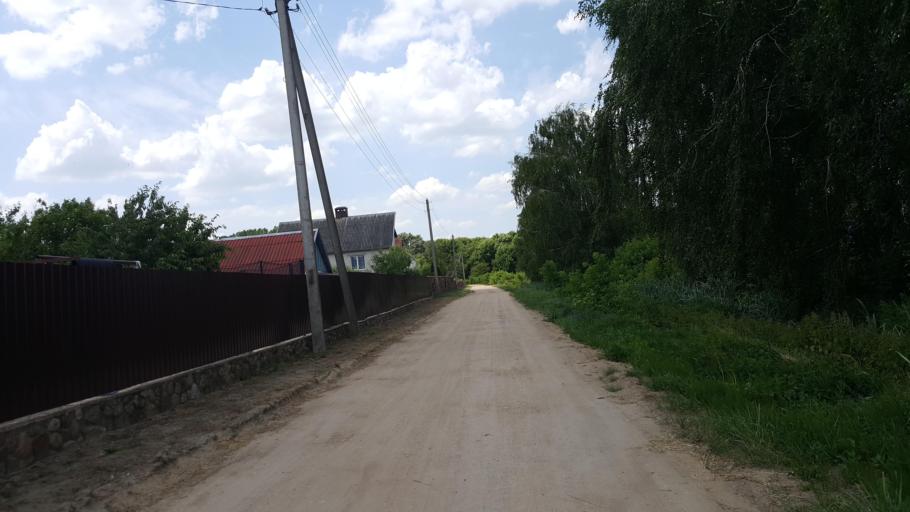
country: BY
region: Brest
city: Kamyanyets
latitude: 52.3975
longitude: 23.8122
